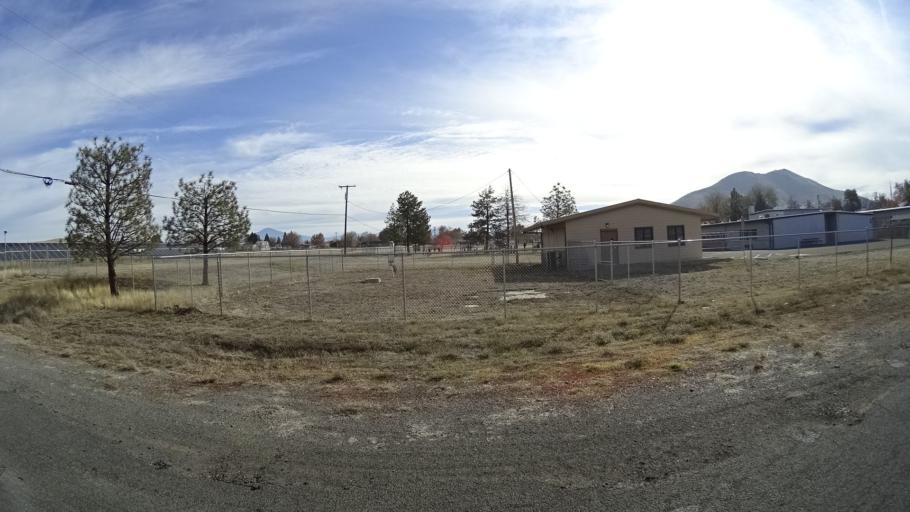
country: US
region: California
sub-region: Siskiyou County
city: Montague
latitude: 41.7286
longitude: -122.5219
